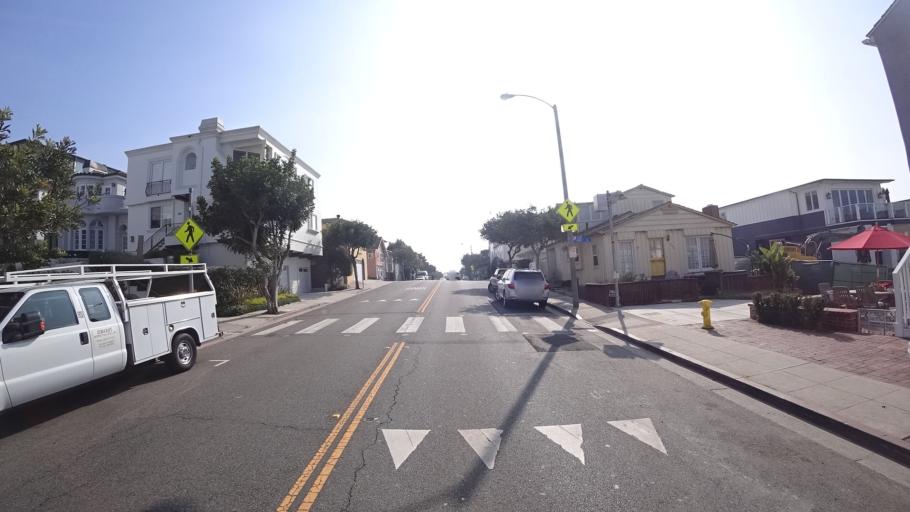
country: US
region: California
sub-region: Los Angeles County
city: Manhattan Beach
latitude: 33.8900
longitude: -118.4126
